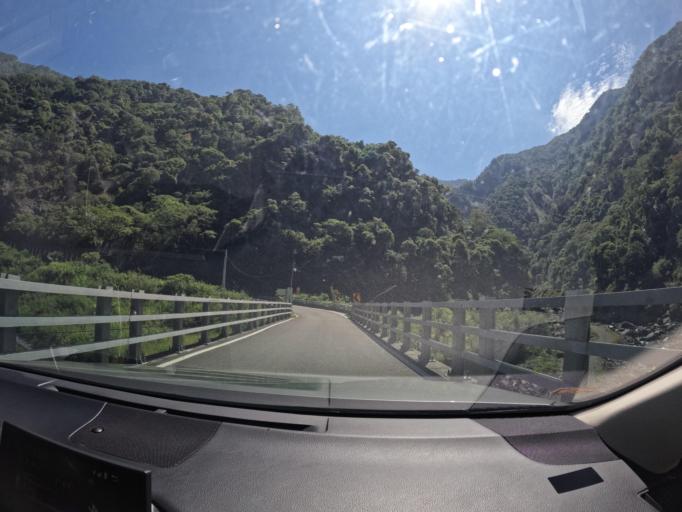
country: TW
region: Taiwan
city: Yujing
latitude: 23.2576
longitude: 120.8495
